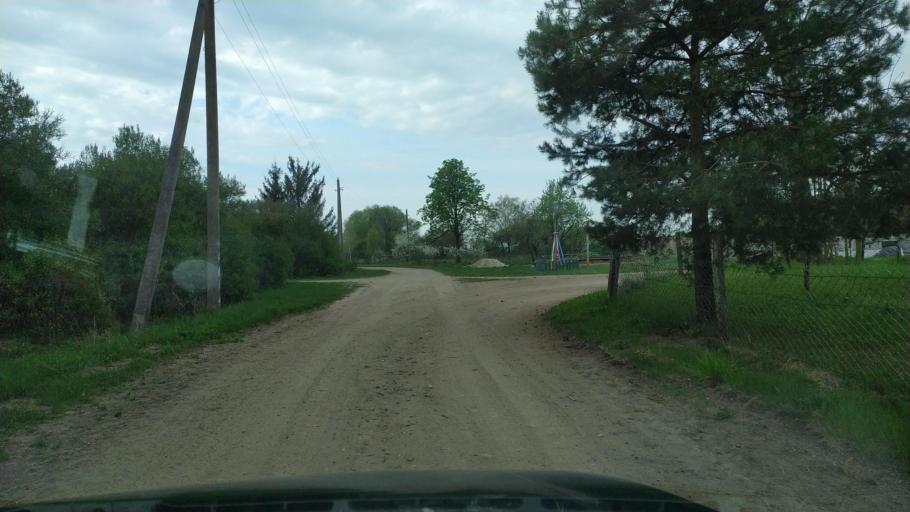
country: BY
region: Brest
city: Zhabinka
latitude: 52.1274
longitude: 24.0904
